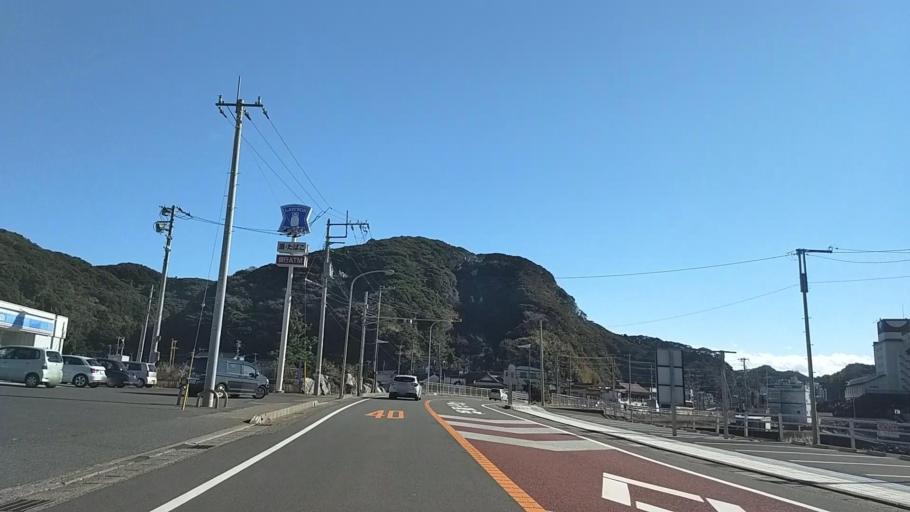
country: JP
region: Chiba
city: Kawaguchi
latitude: 35.1270
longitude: 140.1935
